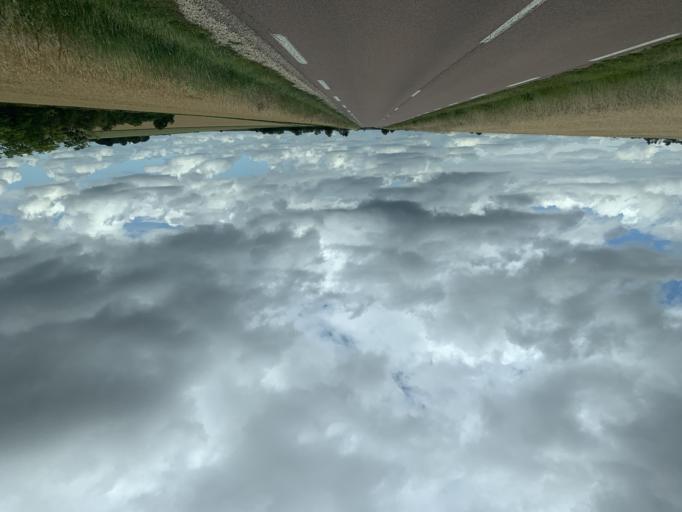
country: FR
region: Bourgogne
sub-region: Departement de l'Yonne
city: Vermenton
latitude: 47.7359
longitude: 3.7232
